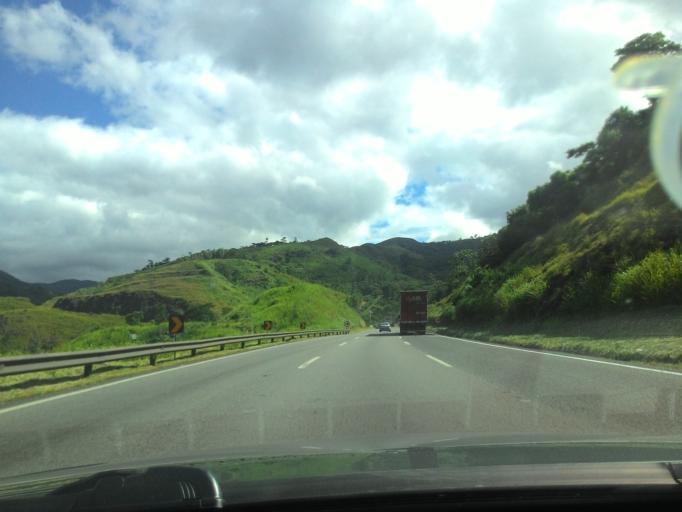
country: BR
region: Sao Paulo
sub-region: Cajati
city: Cajati
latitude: -24.8468
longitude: -48.2193
